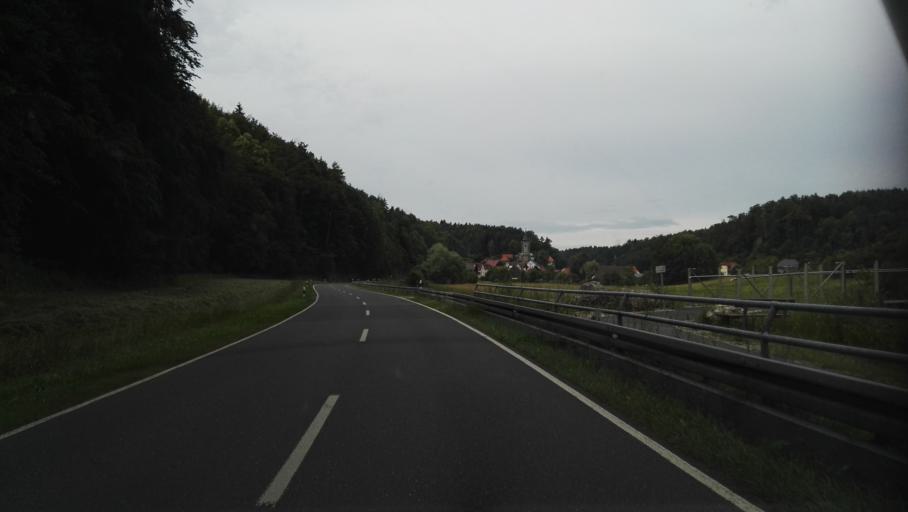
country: DE
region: Bavaria
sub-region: Upper Franconia
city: Waischenfeld
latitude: 49.8588
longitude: 11.3362
